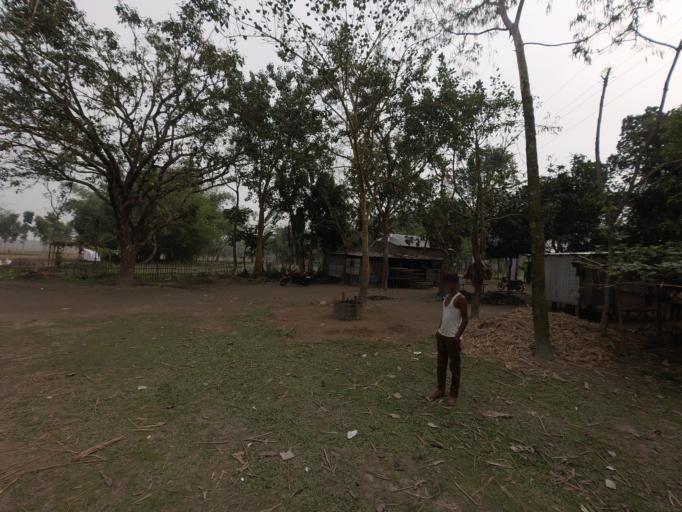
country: BD
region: Rajshahi
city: Saidpur
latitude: 25.9811
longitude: 88.9156
